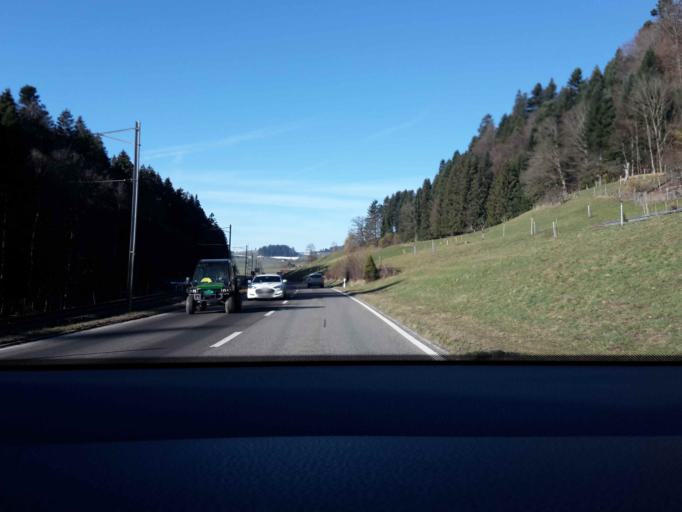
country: CH
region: Bern
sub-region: Emmental District
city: Durrenroth
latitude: 47.0918
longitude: 7.7805
